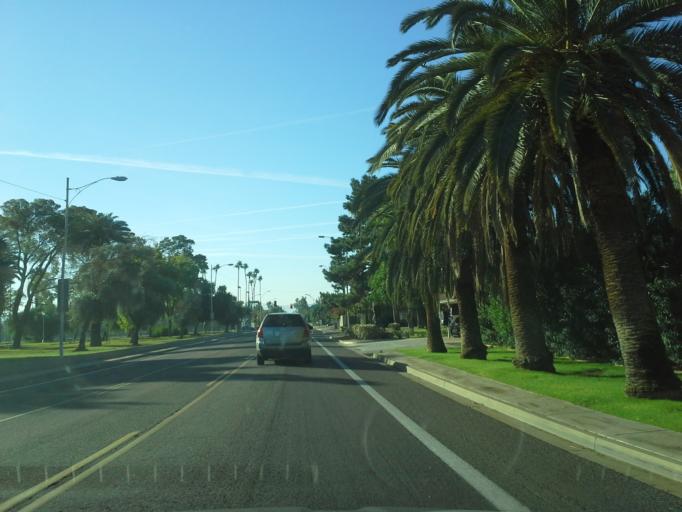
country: US
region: Arizona
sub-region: Maricopa County
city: Phoenix
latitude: 33.4750
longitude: -112.0914
